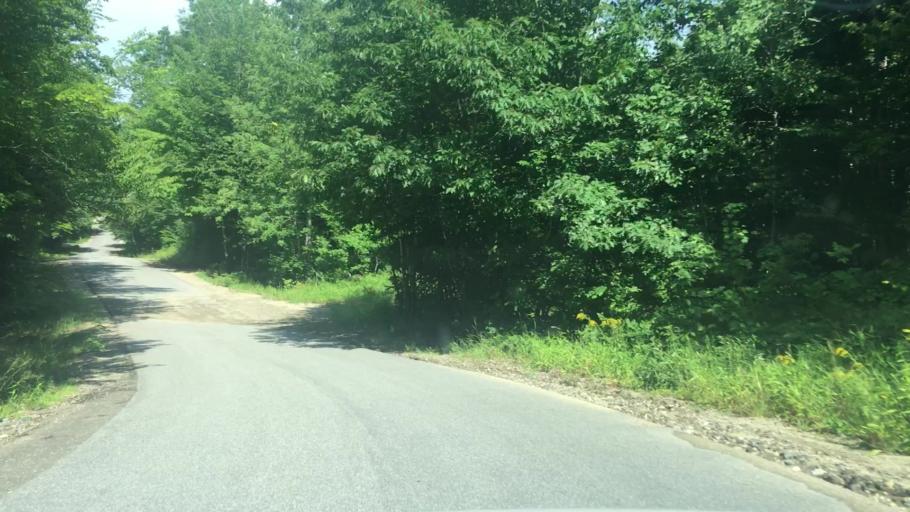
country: US
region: Maine
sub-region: Oxford County
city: West Paris
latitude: 44.3294
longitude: -70.5140
